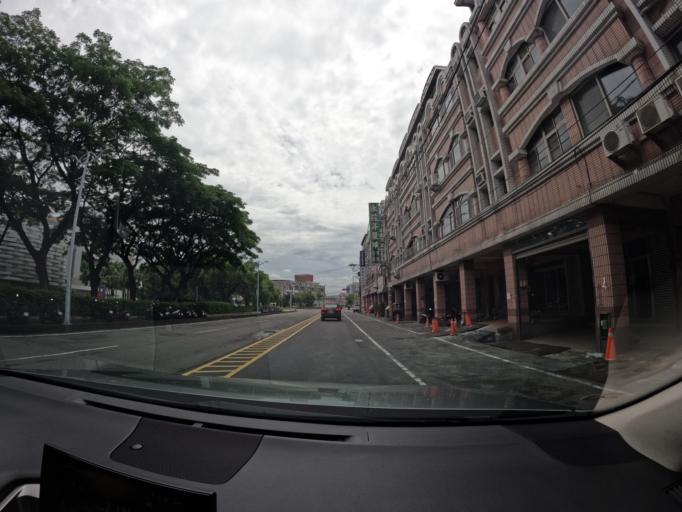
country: TW
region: Kaohsiung
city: Kaohsiung
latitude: 22.7822
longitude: 120.2985
